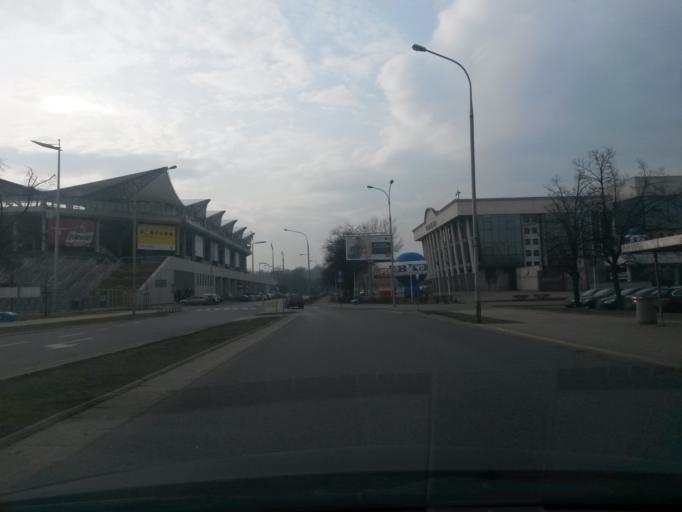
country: PL
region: Masovian Voivodeship
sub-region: Warszawa
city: Srodmiescie
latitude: 52.2215
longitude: 21.0437
